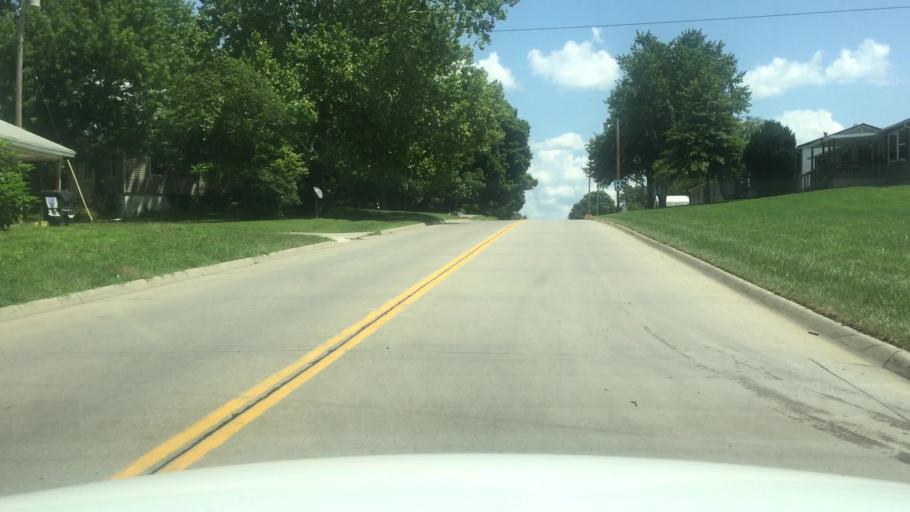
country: US
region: Kansas
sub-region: Brown County
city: Horton
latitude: 39.6673
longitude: -95.5316
